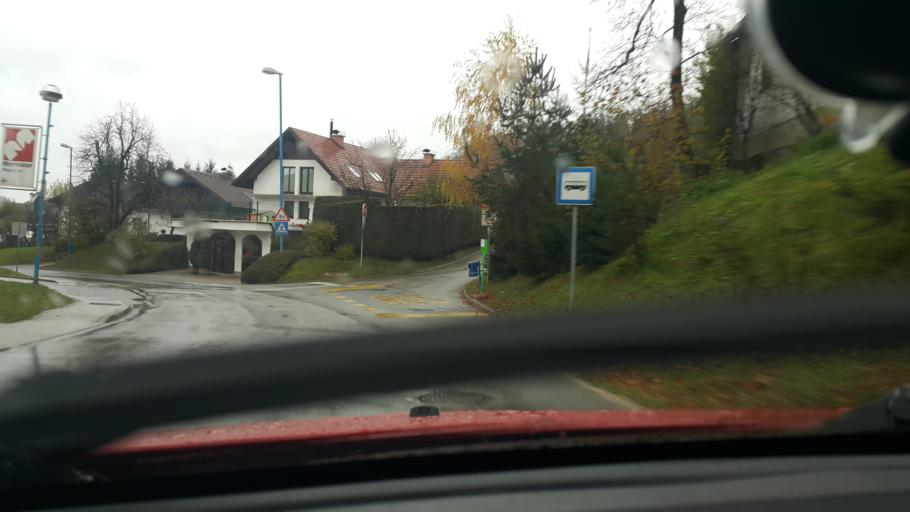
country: SI
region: Medvode
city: Medvode
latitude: 46.1417
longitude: 14.3738
